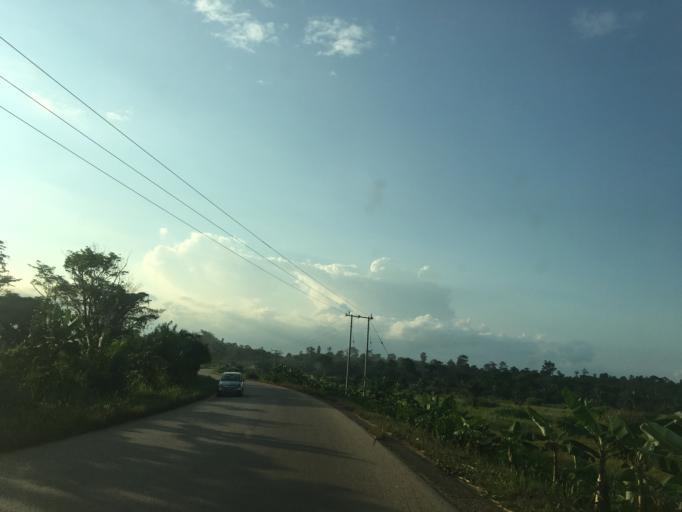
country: GH
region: Western
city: Bibiani
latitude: 6.5736
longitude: -2.3724
